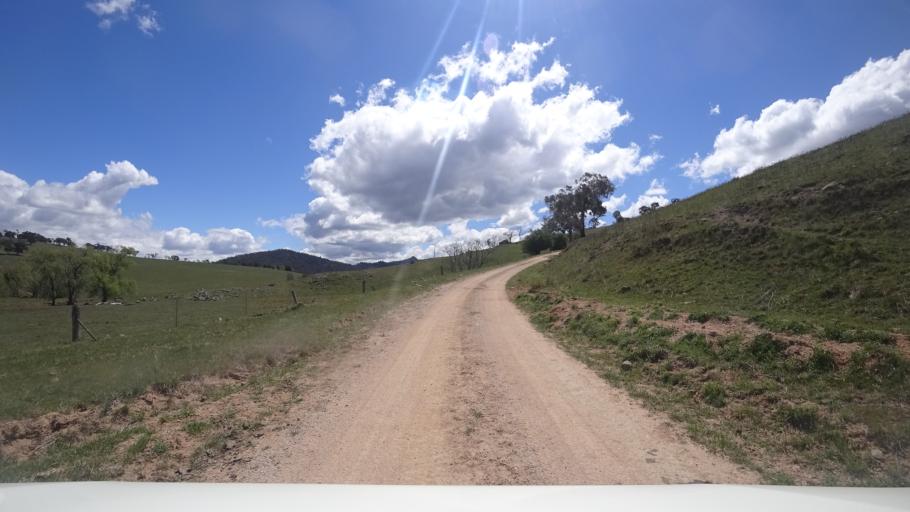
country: AU
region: New South Wales
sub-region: Oberon
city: Oberon
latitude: -33.5753
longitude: 149.9413
